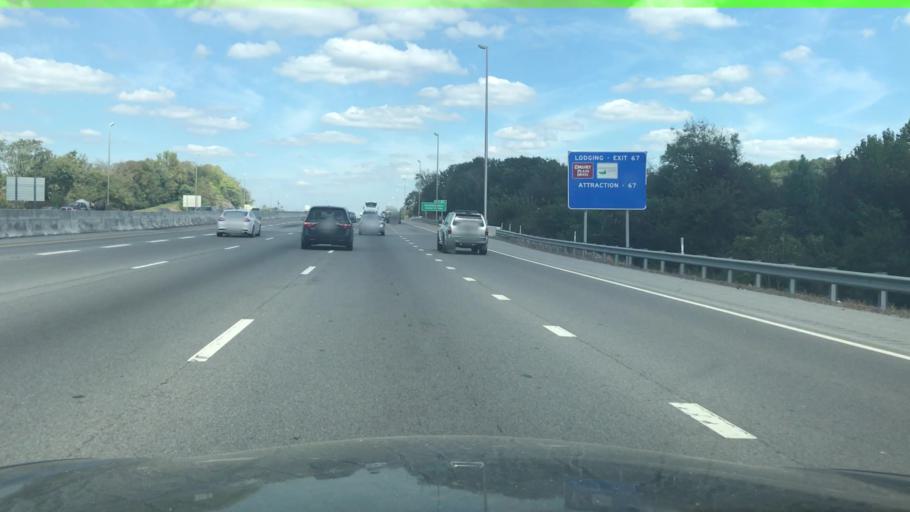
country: US
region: Tennessee
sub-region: Williamson County
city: Franklin
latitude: 35.9254
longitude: -86.8217
